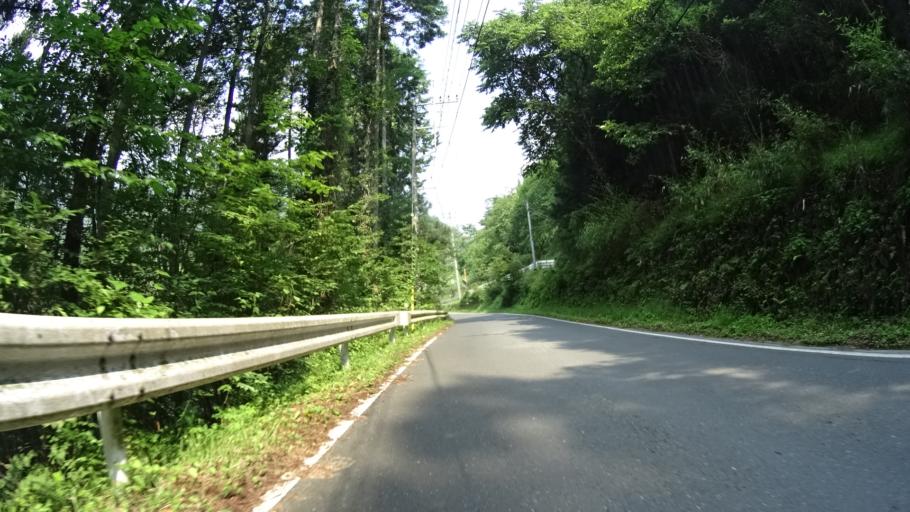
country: JP
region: Saitama
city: Chichibu
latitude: 36.0390
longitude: 138.8989
